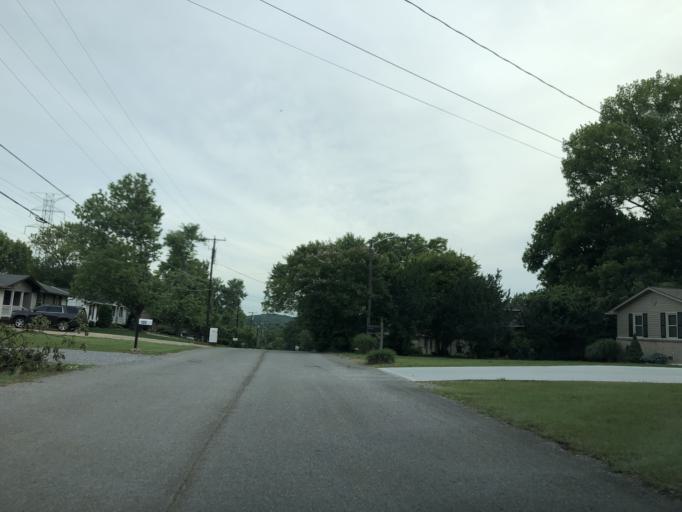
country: US
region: Tennessee
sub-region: Davidson County
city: Goodlettsville
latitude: 36.2944
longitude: -86.7143
